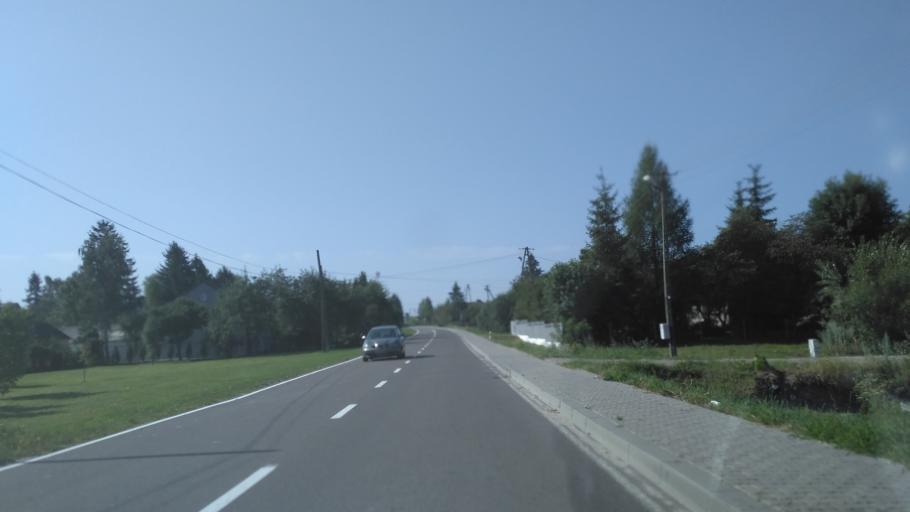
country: PL
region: Lublin Voivodeship
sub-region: Powiat leczynski
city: Cycow
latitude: 51.1925
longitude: 23.1631
